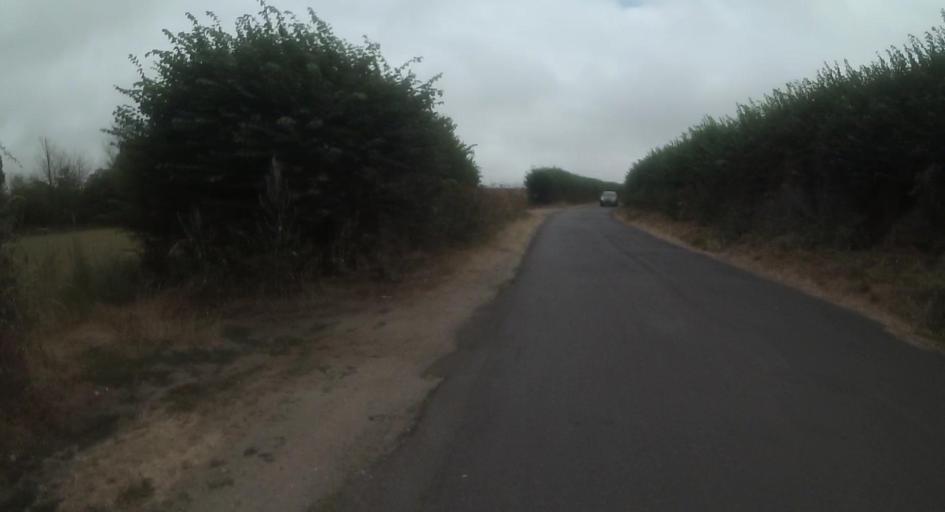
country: GB
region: England
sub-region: Dorset
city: Bovington Camp
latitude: 50.7105
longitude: -2.2922
